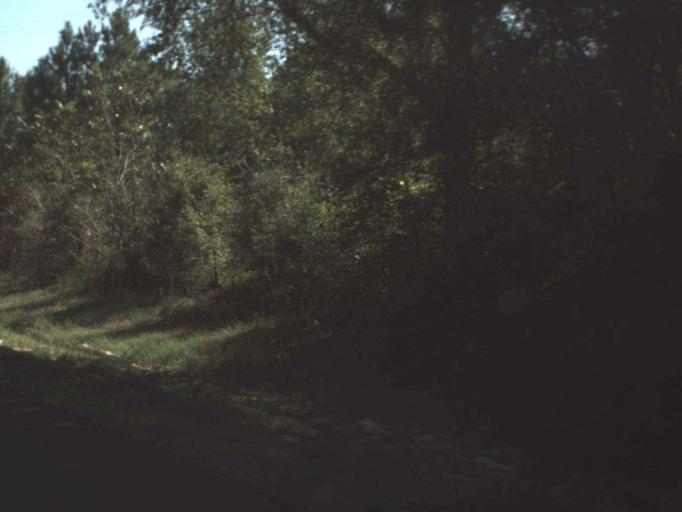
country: US
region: Florida
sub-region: Walton County
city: DeFuniak Springs
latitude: 30.8052
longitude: -86.1972
